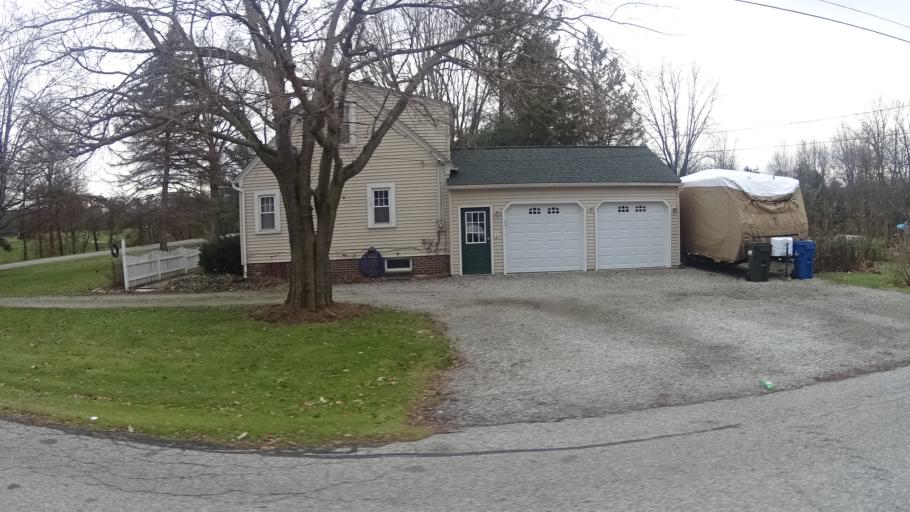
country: US
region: Ohio
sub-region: Cuyahoga County
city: Strongsville
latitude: 41.3049
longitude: -81.8975
